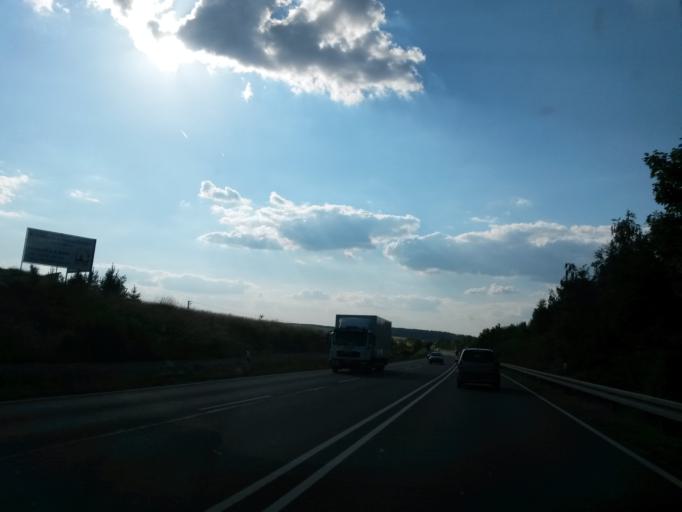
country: DE
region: Bavaria
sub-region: Regierungsbezirk Mittelfranken
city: Diespeck
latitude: 49.5822
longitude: 10.6400
